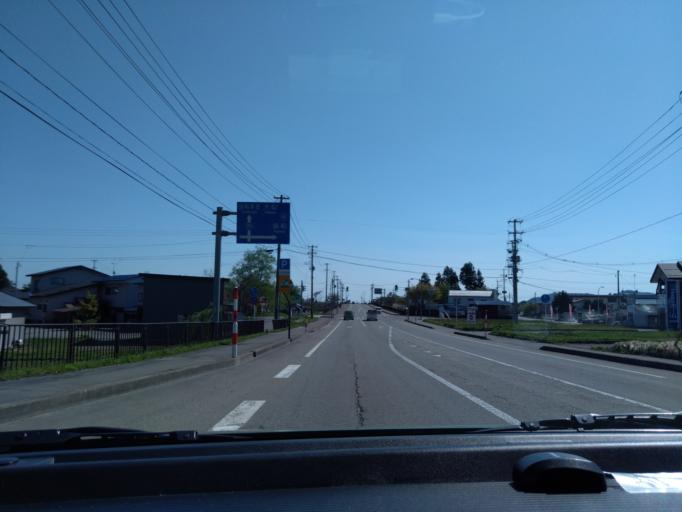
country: JP
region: Akita
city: Kakunodatemachi
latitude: 39.5837
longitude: 140.5699
